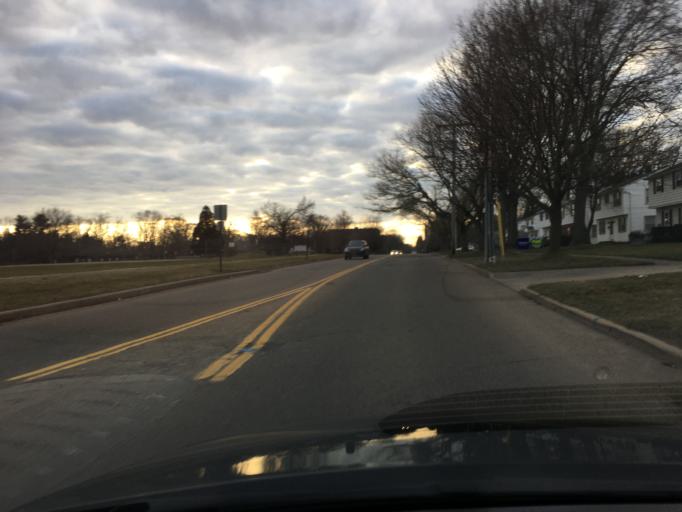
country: US
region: Ohio
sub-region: Summit County
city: Fairlawn
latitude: 41.0997
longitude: -81.5699
